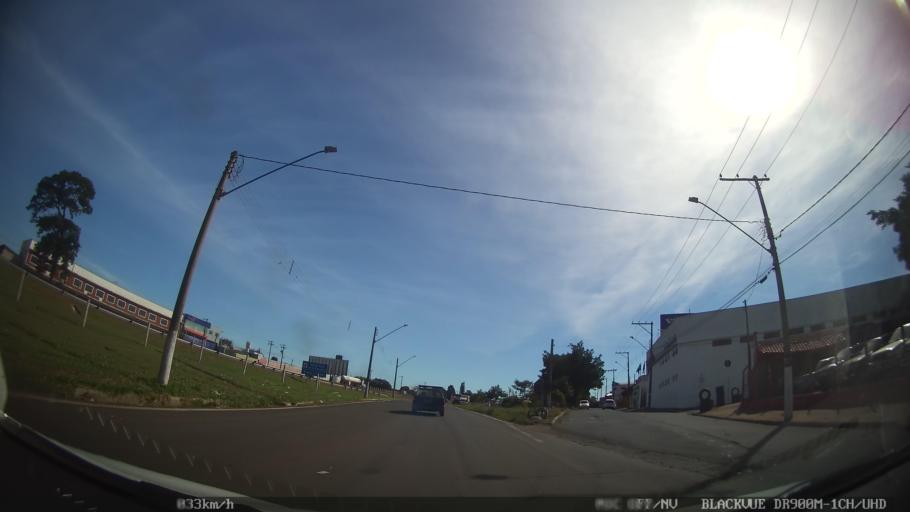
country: BR
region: Sao Paulo
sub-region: Porto Ferreira
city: Porto Ferreira
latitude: -21.8649
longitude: -47.4906
